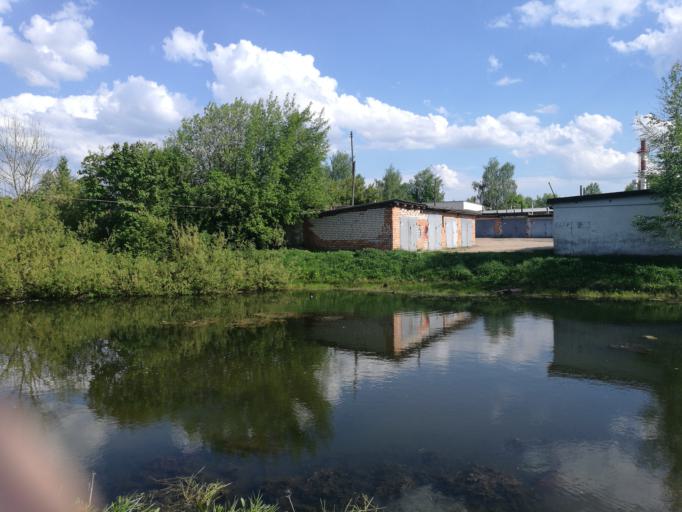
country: BY
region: Minsk
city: Bal'shavik
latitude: 53.9581
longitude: 27.5439
